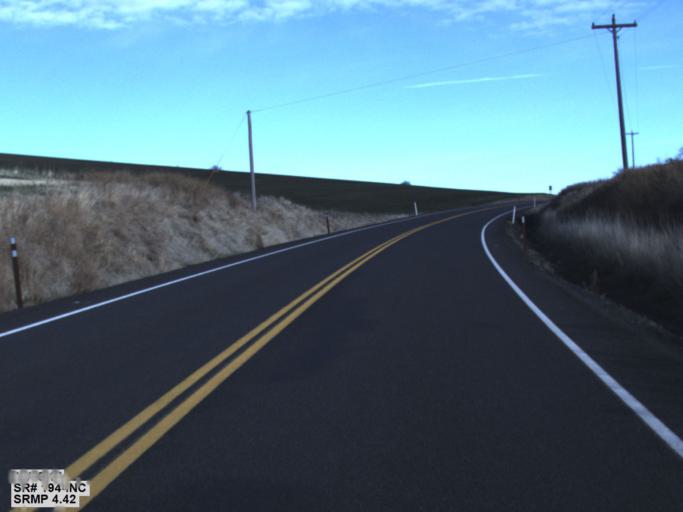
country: US
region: Washington
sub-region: Whitman County
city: Colfax
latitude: 46.7359
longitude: -117.4847
